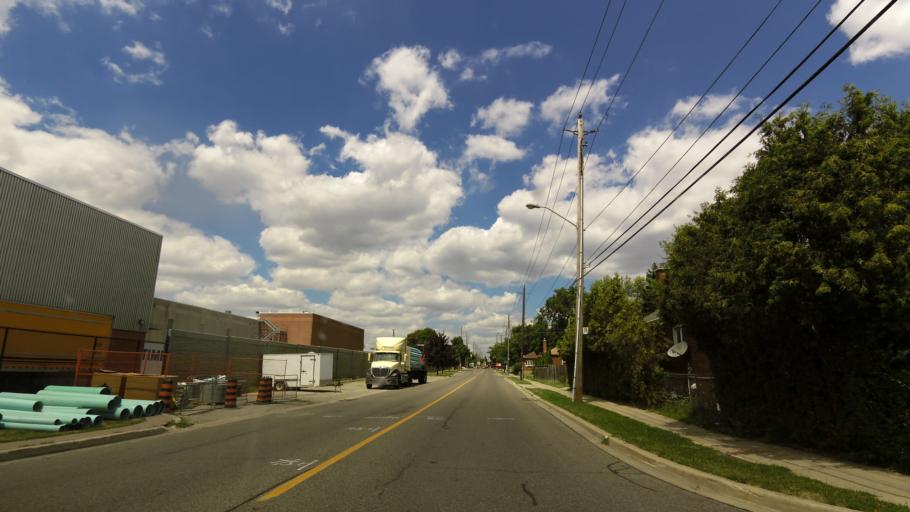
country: CA
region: Ontario
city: Etobicoke
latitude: 43.6065
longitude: -79.4996
